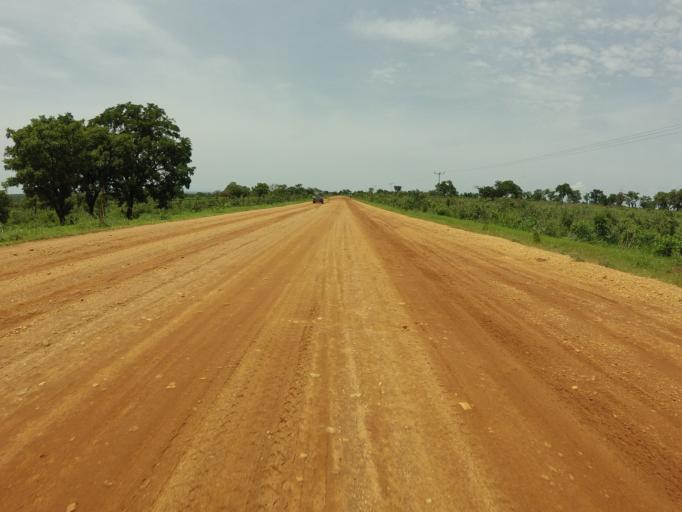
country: GH
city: Kpandae
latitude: 8.7334
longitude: 0.0986
